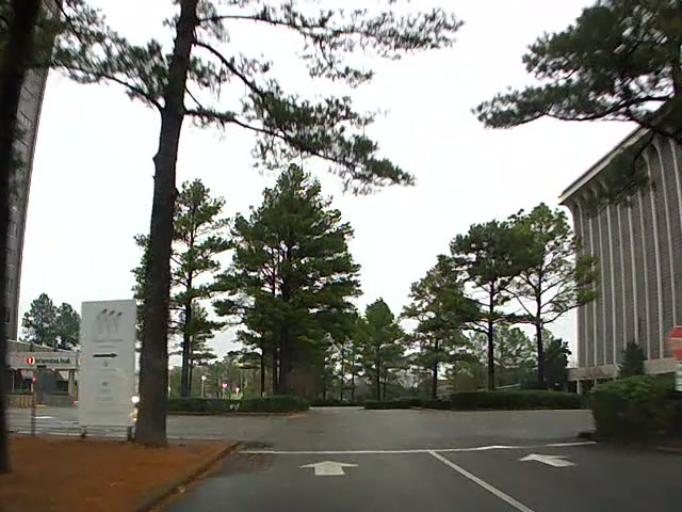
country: US
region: Tennessee
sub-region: Shelby County
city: Germantown
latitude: 35.1130
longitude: -89.8925
